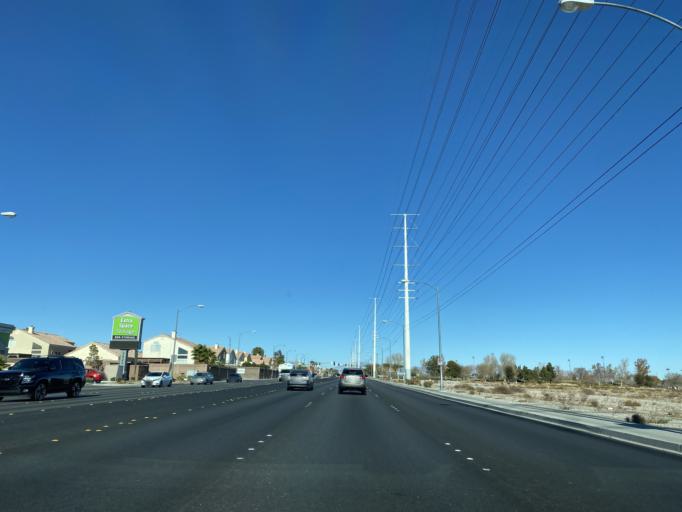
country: US
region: Nevada
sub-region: Clark County
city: Spring Valley
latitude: 36.1195
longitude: -115.2789
